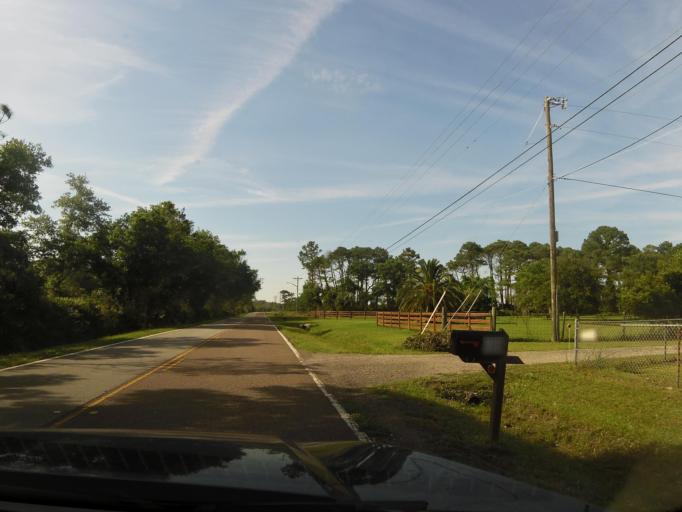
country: US
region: Florida
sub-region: Duval County
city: Atlantic Beach
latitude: 30.4918
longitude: -81.4716
